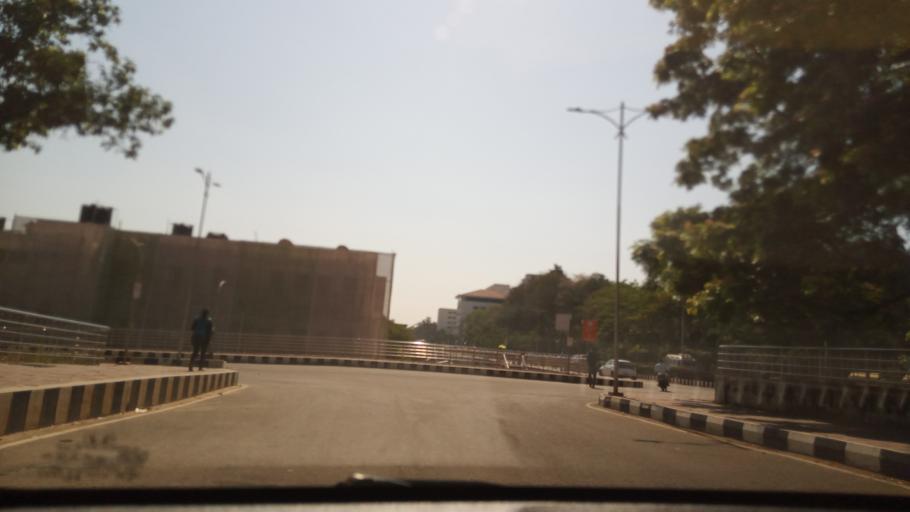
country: IN
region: Karnataka
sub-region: Bangalore Urban
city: Bangalore
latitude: 13.0293
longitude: 77.5665
